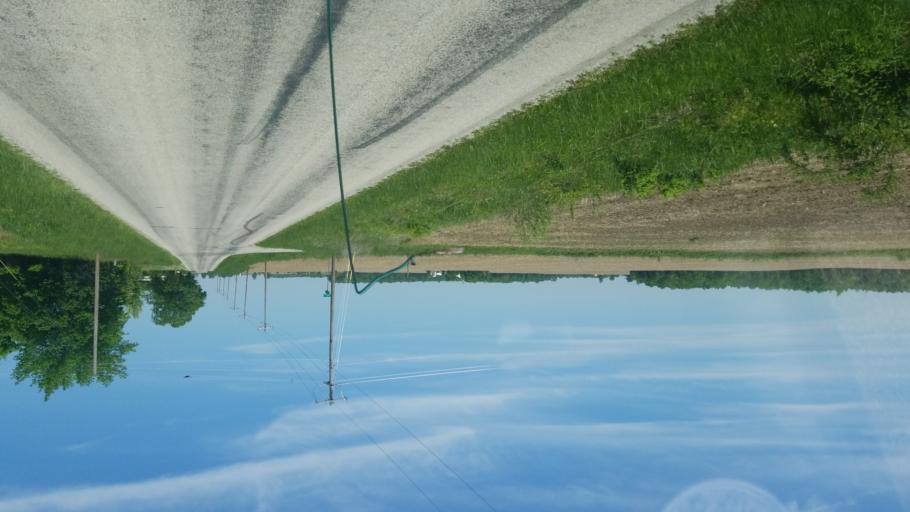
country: US
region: Ohio
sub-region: Huron County
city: Greenwich
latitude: 41.0903
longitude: -82.5371
